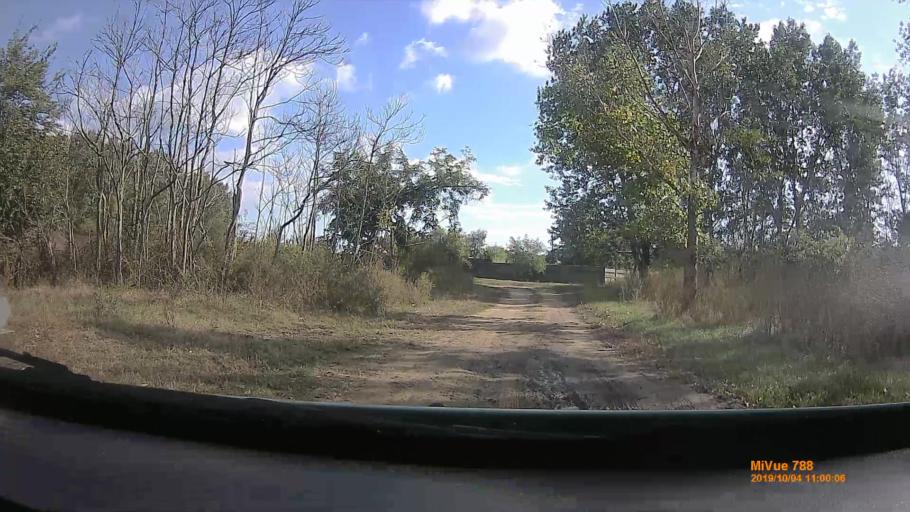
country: HU
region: Szabolcs-Szatmar-Bereg
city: Nyirtelek
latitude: 47.9814
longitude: 21.6698
